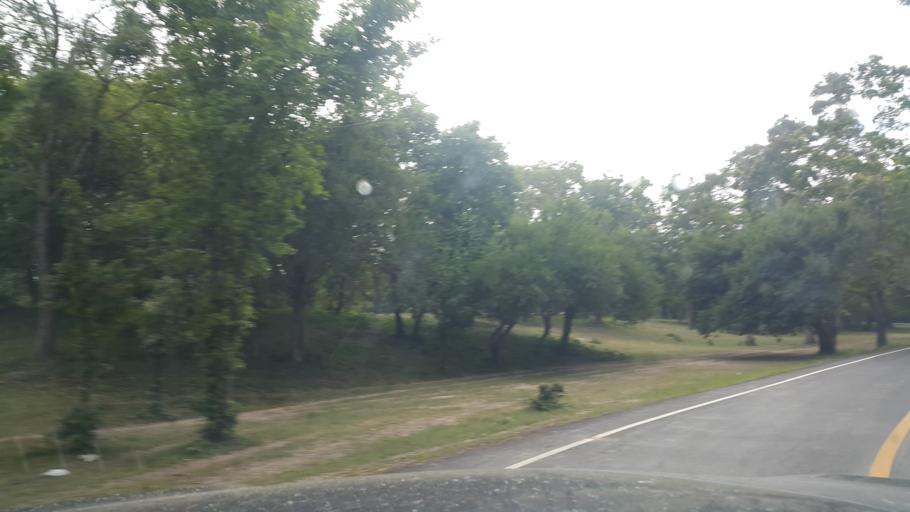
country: TH
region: Sukhothai
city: Ban Na
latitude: 17.0268
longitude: 99.6960
